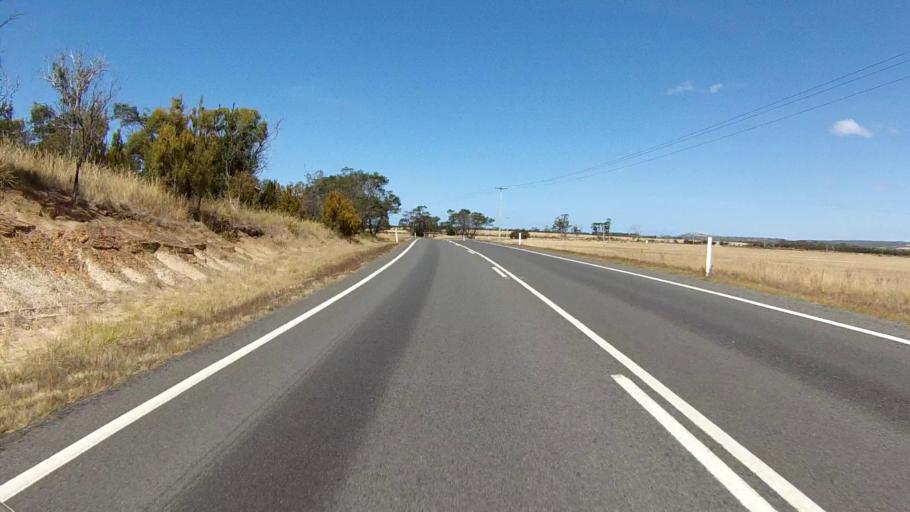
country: AU
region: Tasmania
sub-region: Break O'Day
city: St Helens
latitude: -42.0865
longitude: 148.0655
